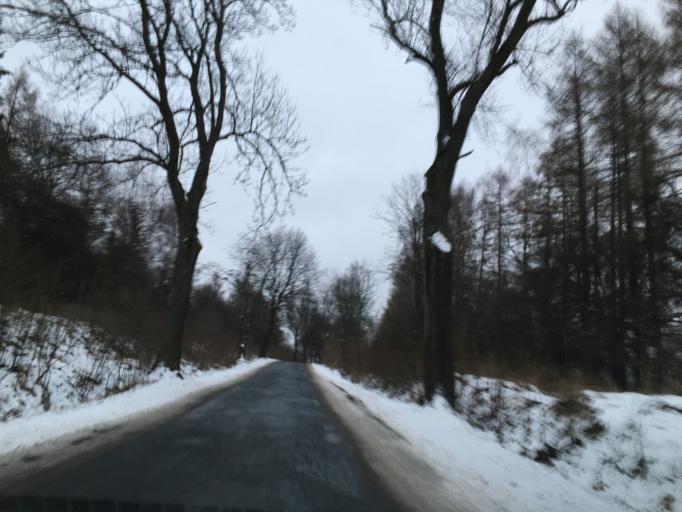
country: PL
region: Lower Silesian Voivodeship
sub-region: Powiat kamiennogorski
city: Krzeszow
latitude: 50.6550
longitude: 16.0629
